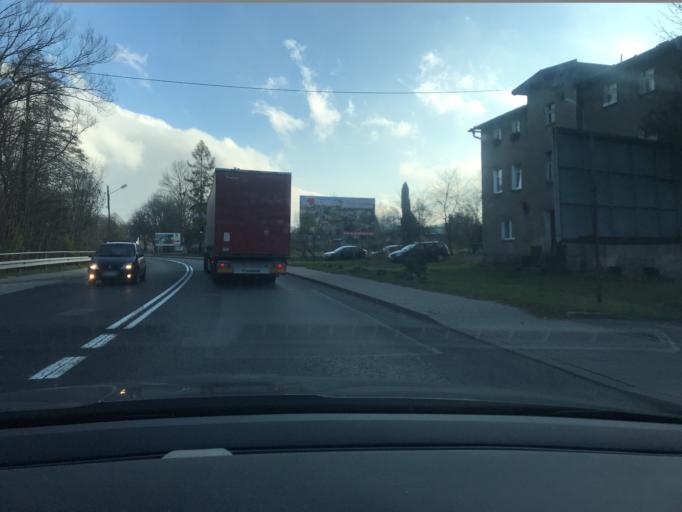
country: PL
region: Lower Silesian Voivodeship
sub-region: Powiat klodzki
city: Kudowa-Zdroj
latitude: 50.4307
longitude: 16.2454
